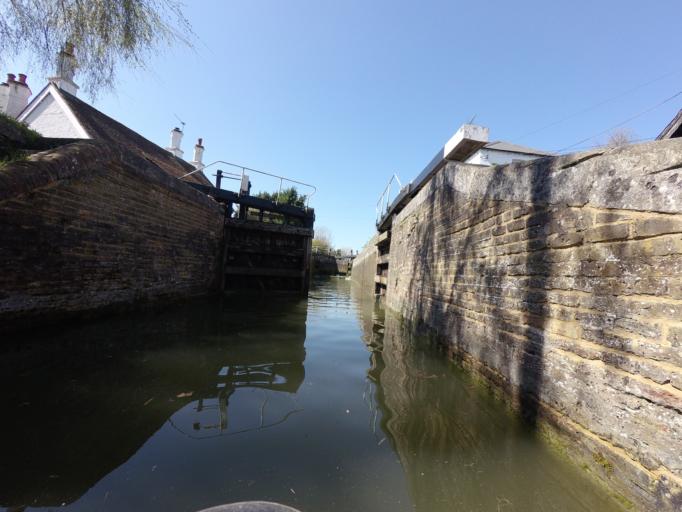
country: GB
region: England
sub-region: Hertfordshire
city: Tring
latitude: 51.7834
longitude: -0.6119
